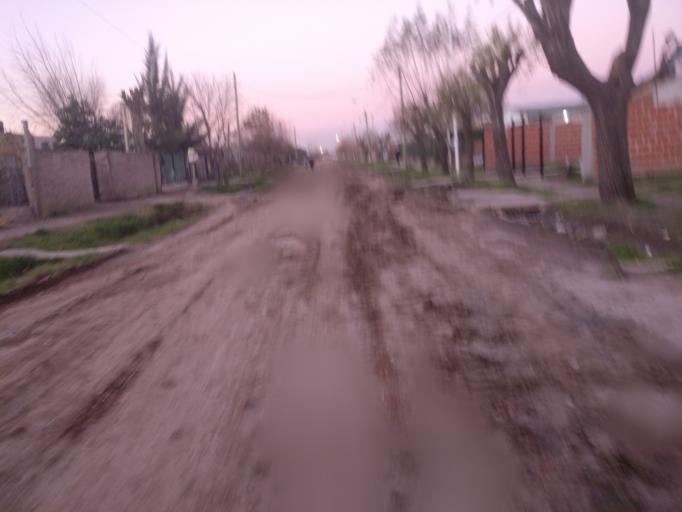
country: AR
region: Buenos Aires
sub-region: Partido de Ezeiza
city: Ezeiza
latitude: -34.9392
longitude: -58.6079
